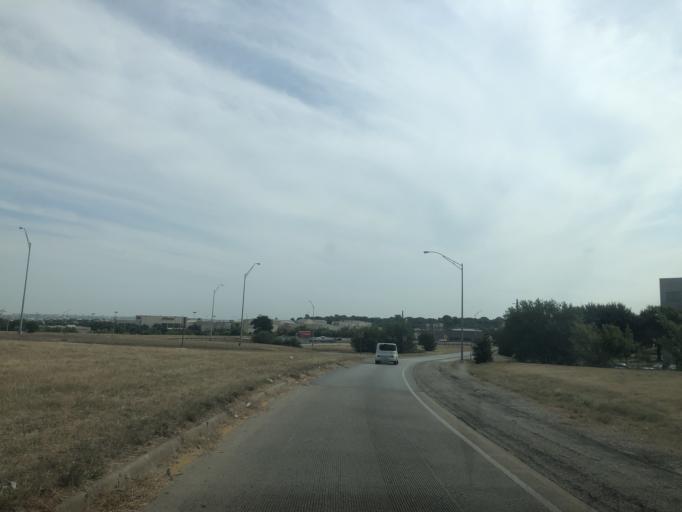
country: US
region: Texas
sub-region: Tarrant County
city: White Settlement
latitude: 32.7345
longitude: -97.4404
